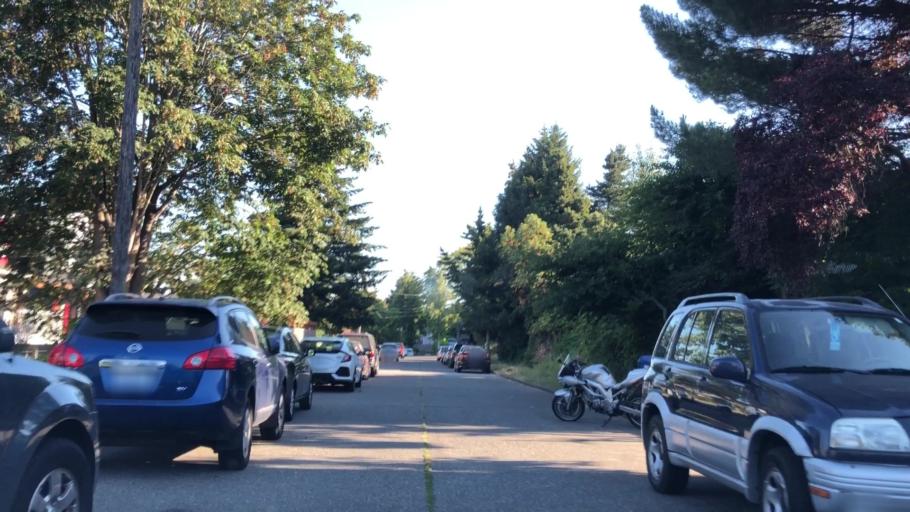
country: US
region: Washington
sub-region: King County
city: White Center
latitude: 47.5345
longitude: -122.3517
